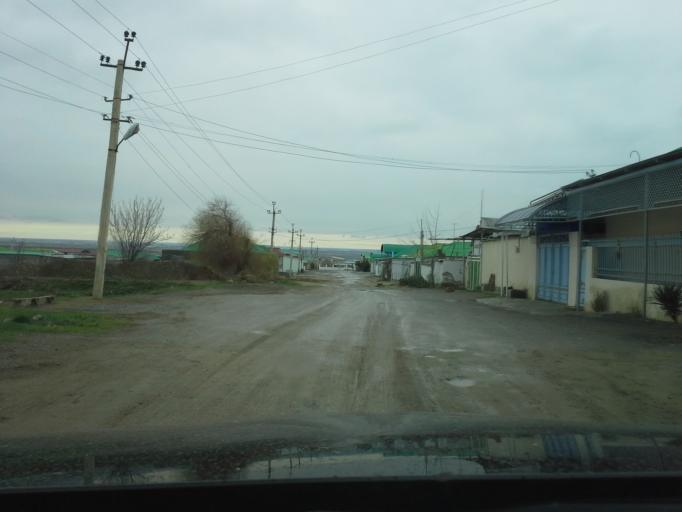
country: TM
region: Ahal
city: Abadan
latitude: 37.9581
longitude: 58.2016
